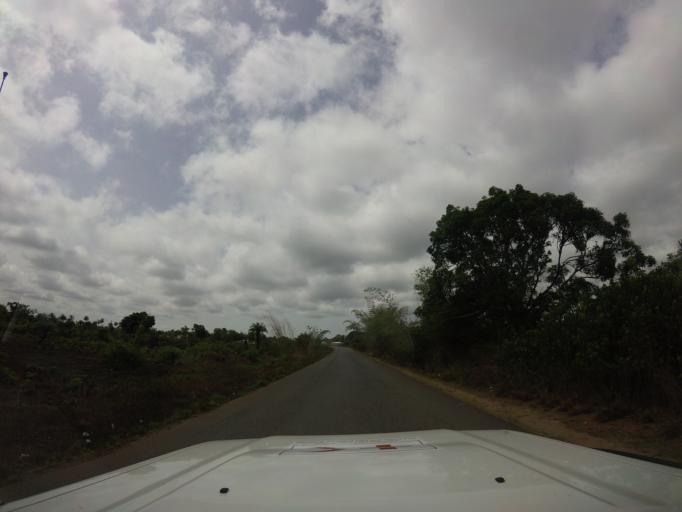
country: LR
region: Montserrado
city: Monrovia
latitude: 6.4898
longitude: -10.8124
